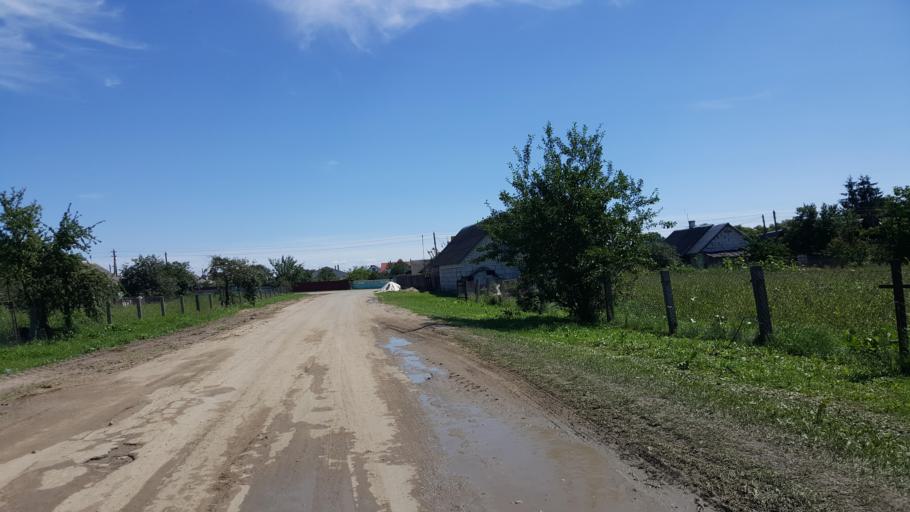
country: BY
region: Brest
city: Charnawchytsy
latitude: 52.2244
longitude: 23.7373
